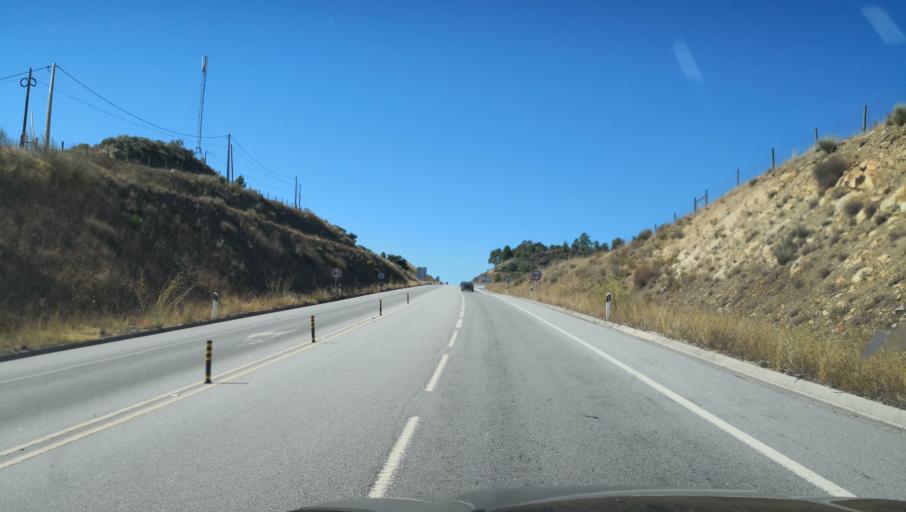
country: PT
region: Vila Real
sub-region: Valpacos
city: Valpacos
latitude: 41.5668
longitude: -7.2739
